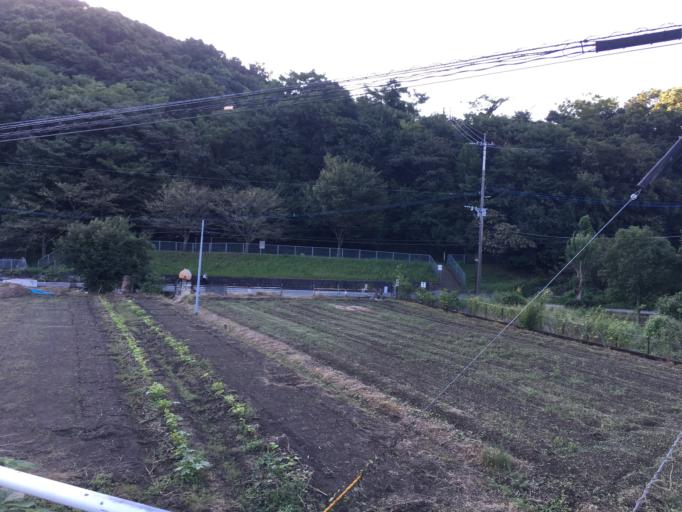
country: JP
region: Kumamoto
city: Kumamoto
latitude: 32.7884
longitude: 130.6645
